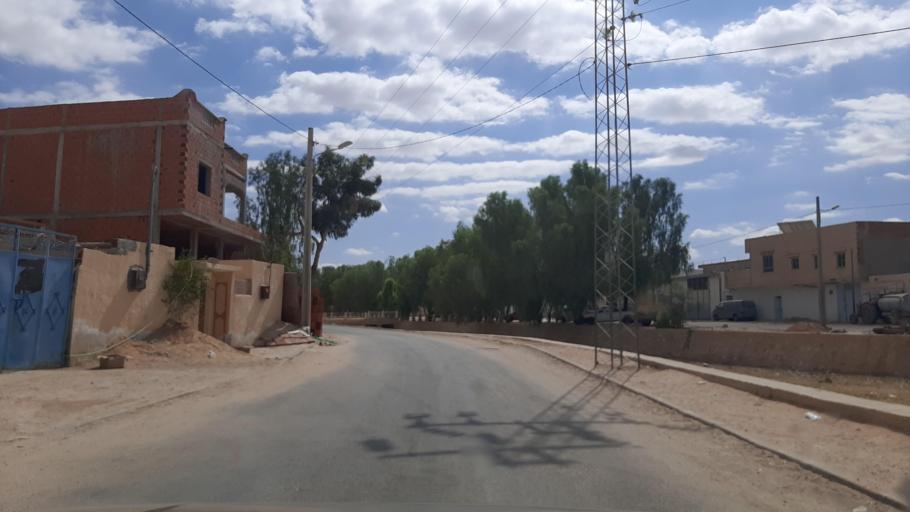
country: TN
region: Tataouine
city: Tataouine
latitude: 32.9264
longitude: 10.4586
